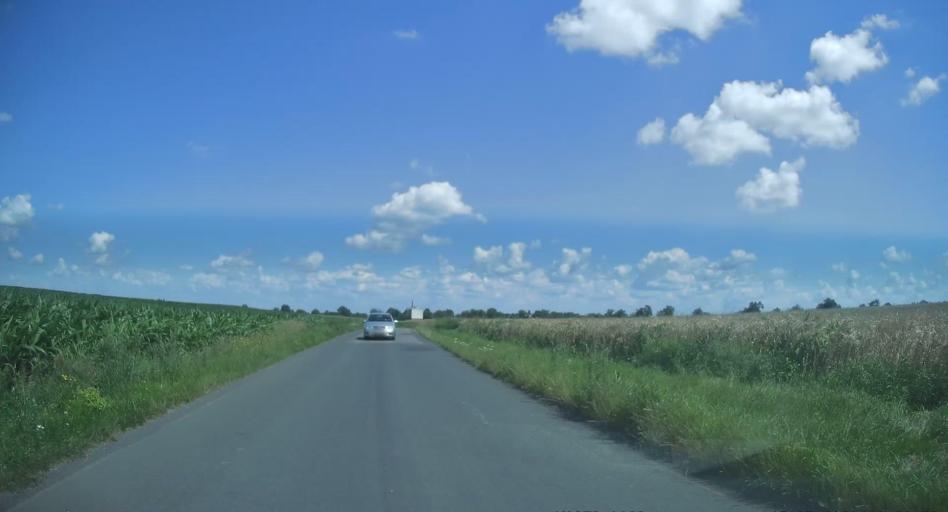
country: PL
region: Subcarpathian Voivodeship
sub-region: Powiat jaroslawski
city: Sosnica
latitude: 49.8543
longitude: 22.8789
